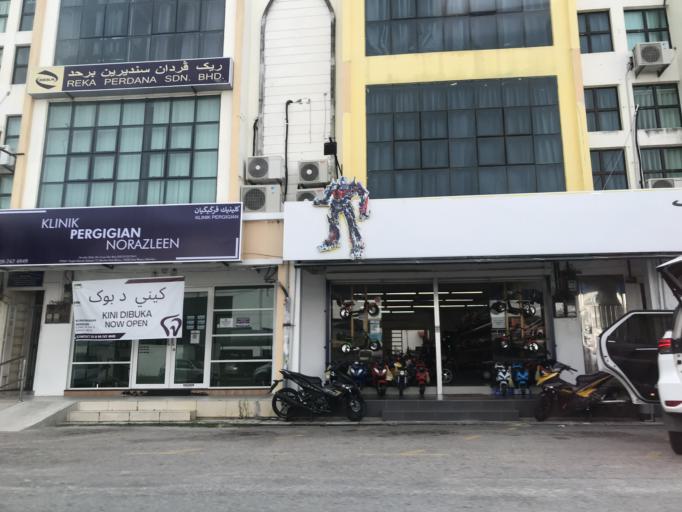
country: MY
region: Kelantan
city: Kota Bharu
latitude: 6.1148
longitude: 102.2309
